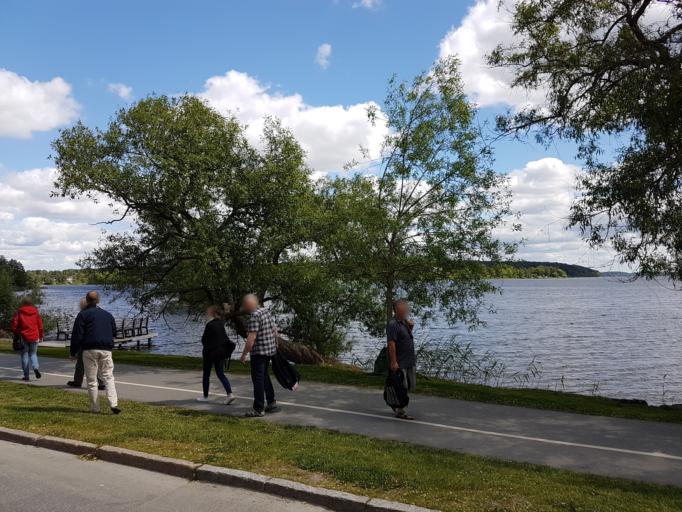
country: SE
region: Stockholm
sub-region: Sigtuna Kommun
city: Sigtuna
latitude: 59.6142
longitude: 17.7201
